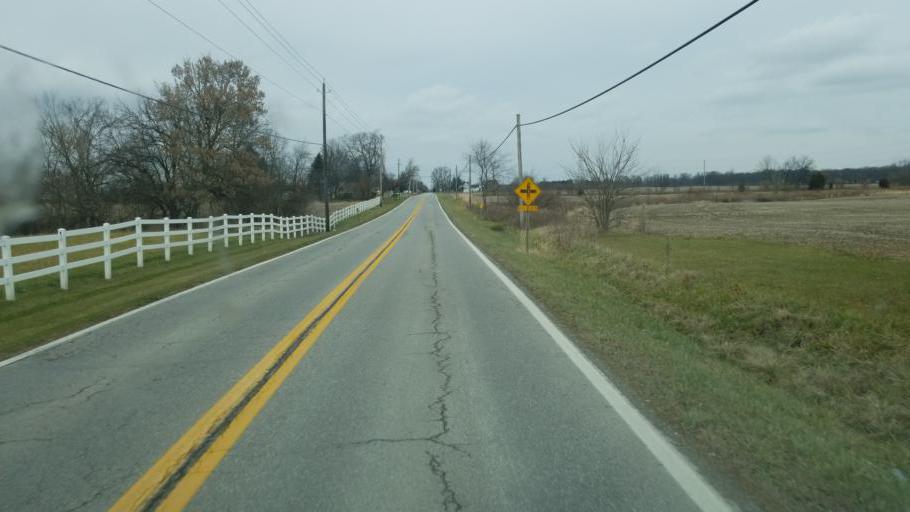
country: US
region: Ohio
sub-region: Delaware County
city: Delaware
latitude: 40.2350
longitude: -83.1317
